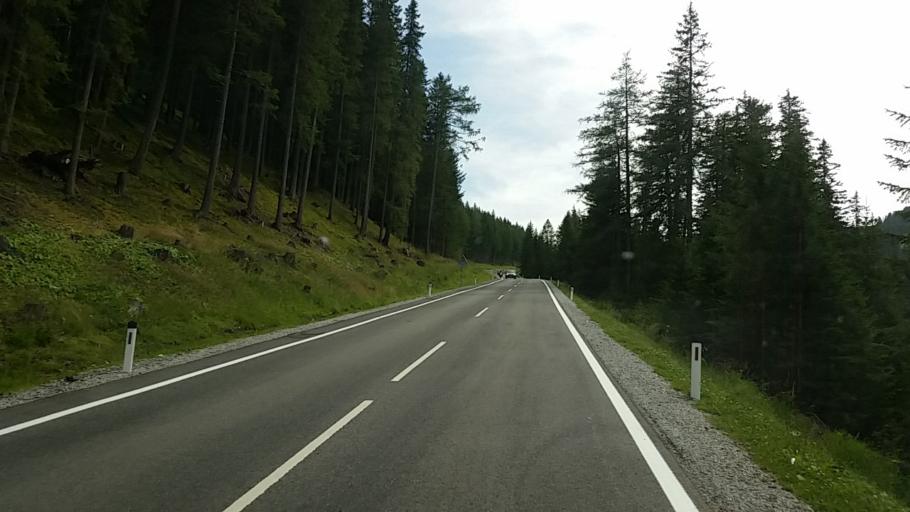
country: AT
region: Salzburg
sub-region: Politischer Bezirk Tamsweg
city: Sankt Michael im Lungau
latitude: 47.0662
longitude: 13.6155
